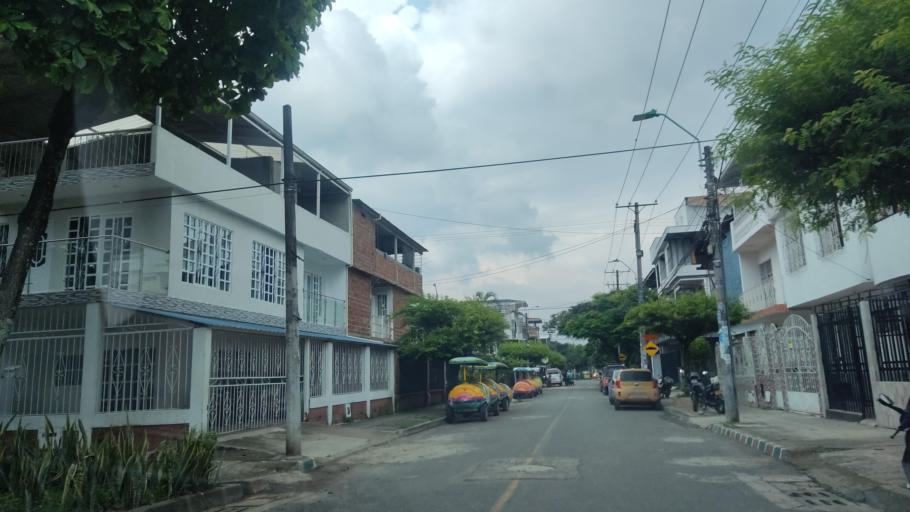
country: CO
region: Valle del Cauca
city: Cali
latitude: 3.4014
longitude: -76.5023
